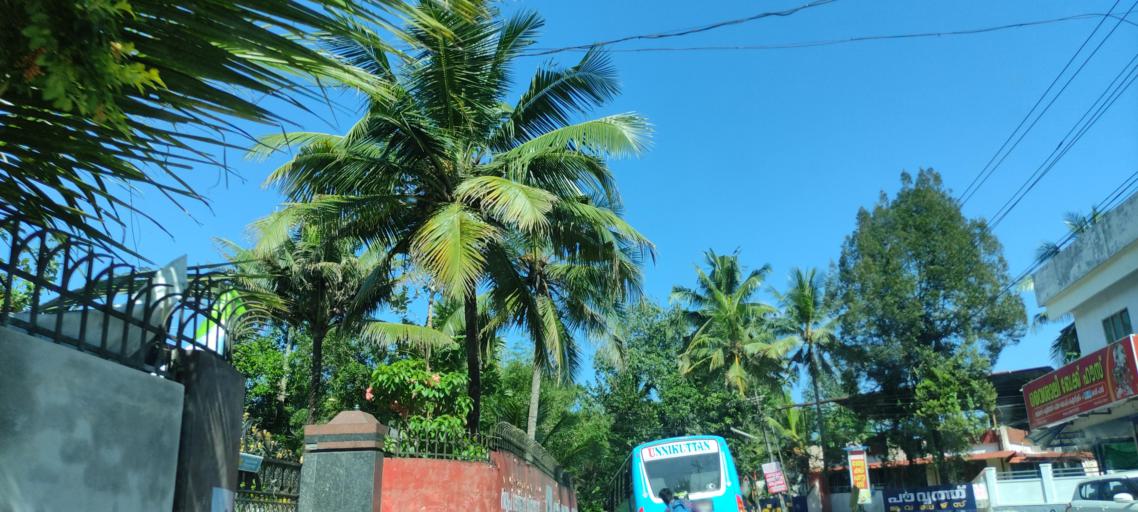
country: IN
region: Kerala
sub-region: Pattanamtitta
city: Adur
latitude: 9.1573
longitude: 76.7423
